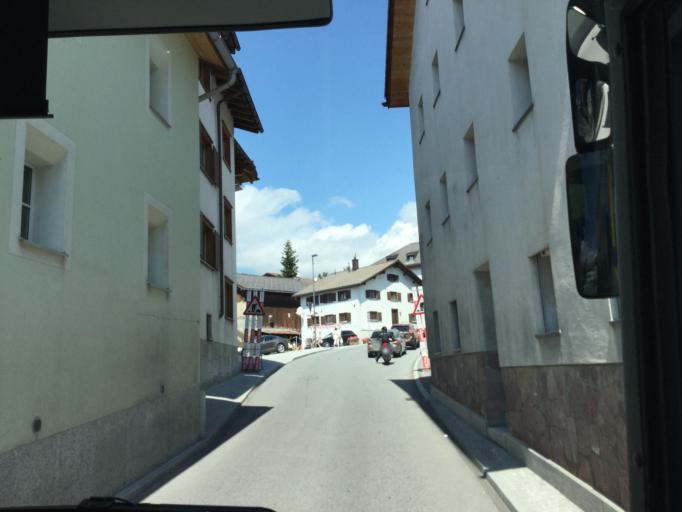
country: CH
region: Grisons
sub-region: Albula District
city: Tiefencastel
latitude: 46.6842
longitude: 9.5637
